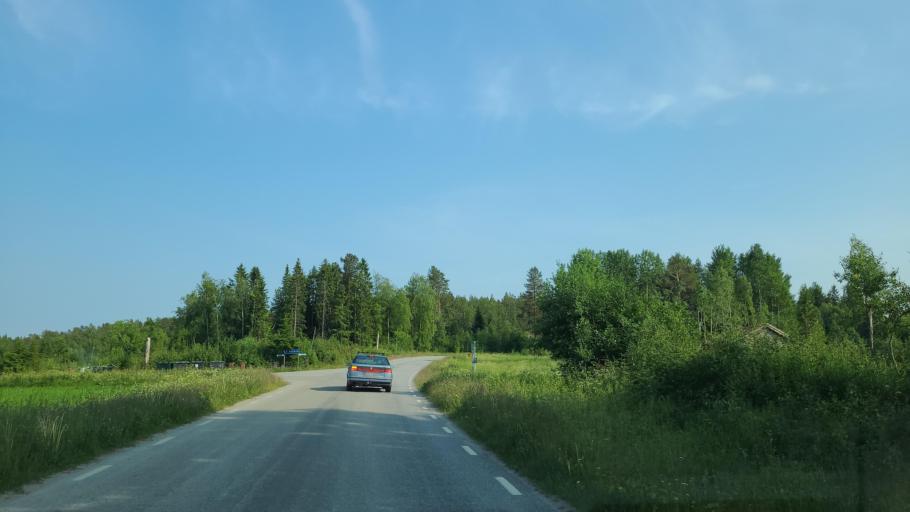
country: SE
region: Vaesterbotten
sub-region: Skelleftea Kommun
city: Burea
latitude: 64.3437
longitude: 21.3430
